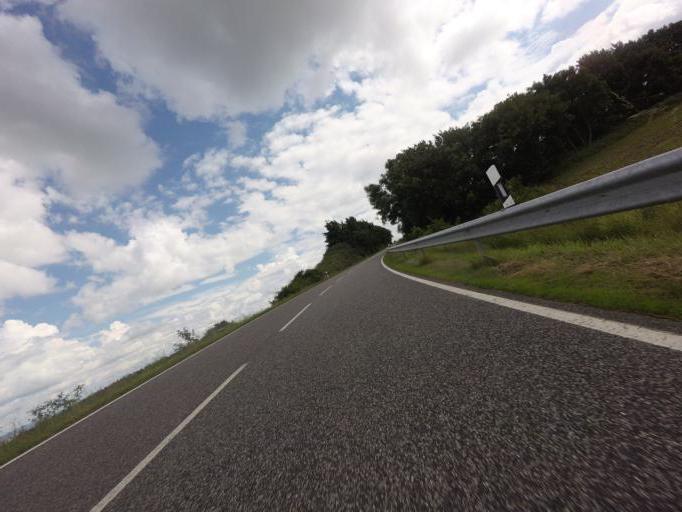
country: DE
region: Rheinland-Pfalz
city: Monreal
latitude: 50.2891
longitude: 7.1512
